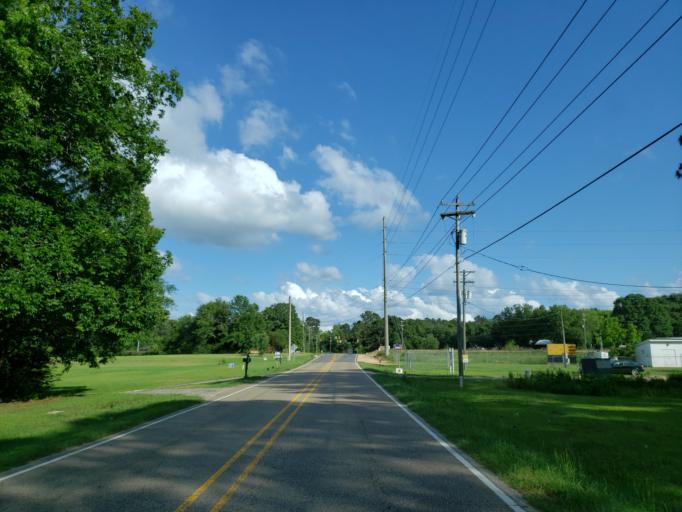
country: US
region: Mississippi
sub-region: Lamar County
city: West Hattiesburg
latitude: 31.2728
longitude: -89.4138
